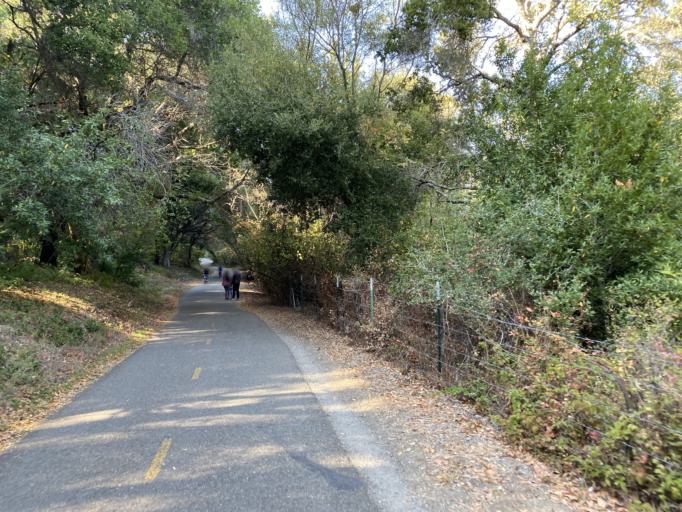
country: US
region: California
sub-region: San Mateo County
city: Hillsborough
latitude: 37.5759
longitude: -122.4083
